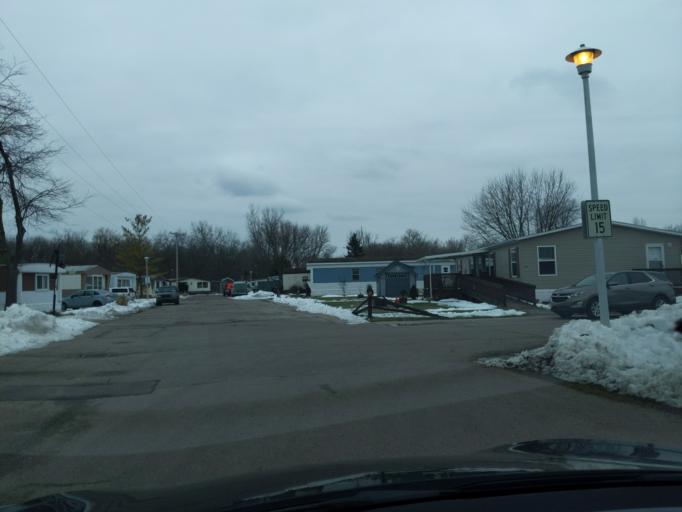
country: US
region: Michigan
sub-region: Ingham County
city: Lansing
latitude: 42.7735
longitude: -84.5504
